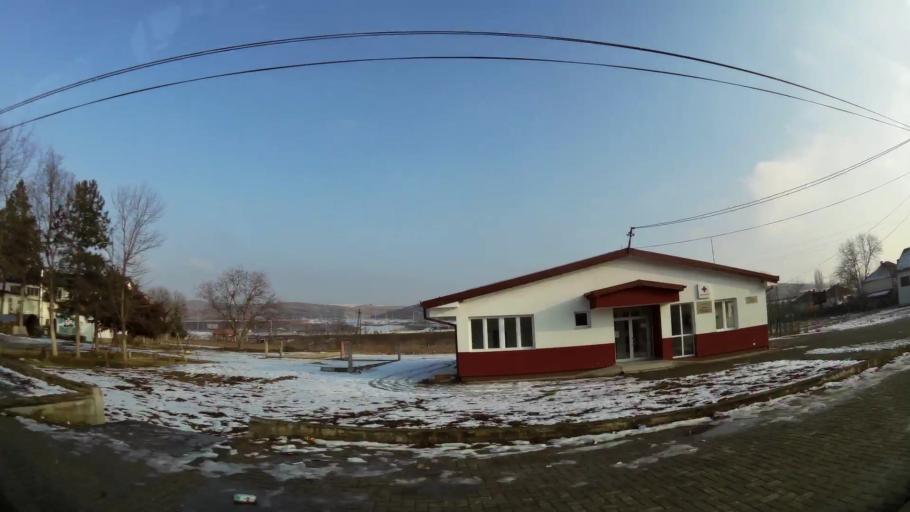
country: MK
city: Miladinovci
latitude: 41.9877
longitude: 21.6521
